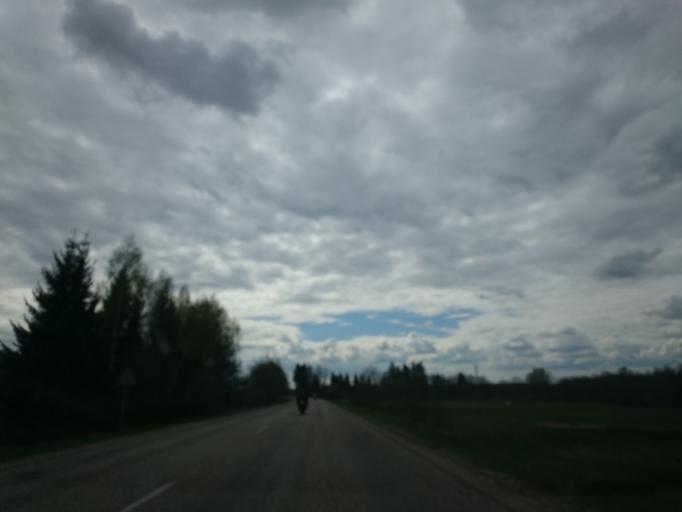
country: LV
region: Aizpute
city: Aizpute
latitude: 56.7814
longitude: 21.6400
